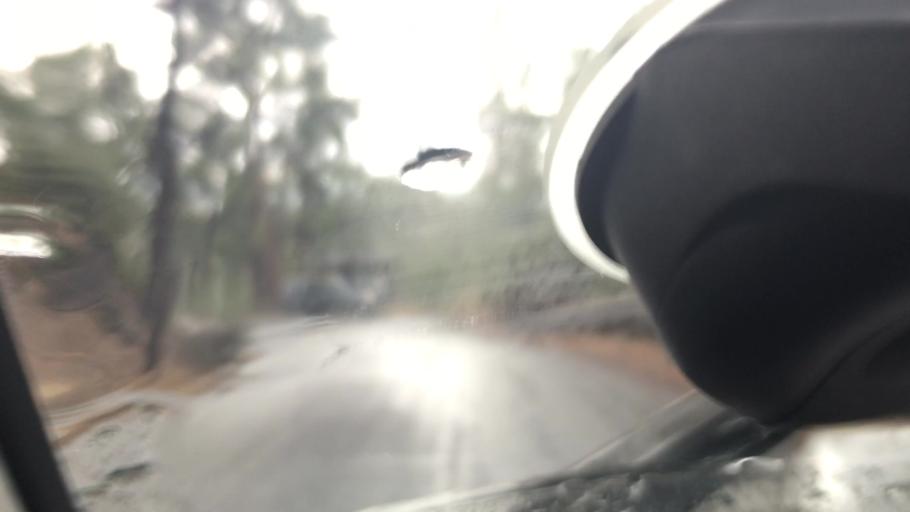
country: US
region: Arizona
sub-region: Yavapai County
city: Prescott
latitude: 34.5082
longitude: -112.3830
